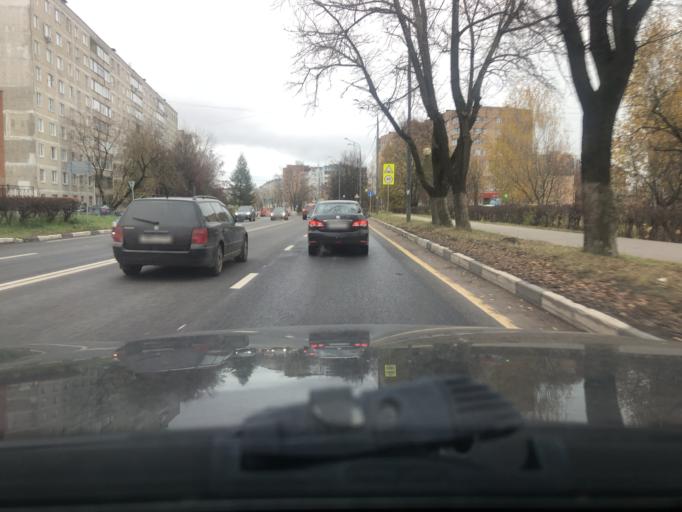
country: RU
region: Moskovskaya
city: Sergiyev Posad
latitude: 56.3285
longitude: 38.1319
